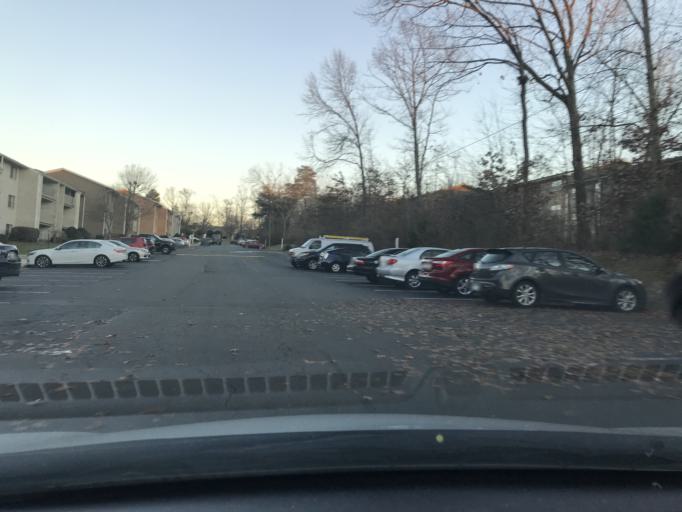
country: US
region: Virginia
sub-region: City of Fairfax
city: Fairfax
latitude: 38.8628
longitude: -77.3290
